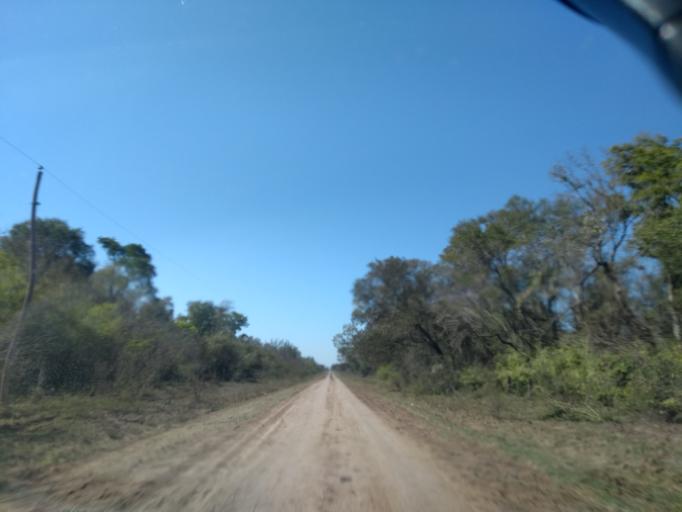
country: AR
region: Chaco
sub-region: Departamento de Quitilipi
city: Quitilipi
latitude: -26.7101
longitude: -60.2110
